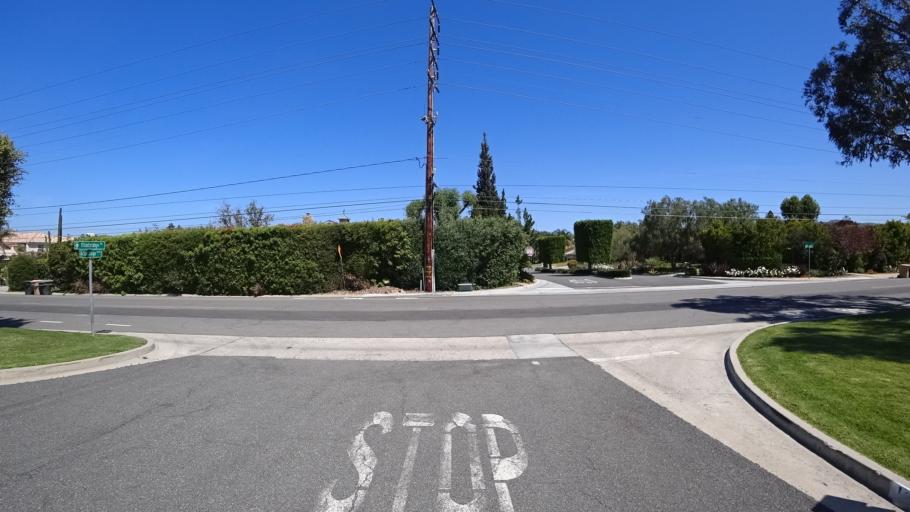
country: US
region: California
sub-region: Orange County
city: Villa Park
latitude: 33.8142
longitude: -117.8075
